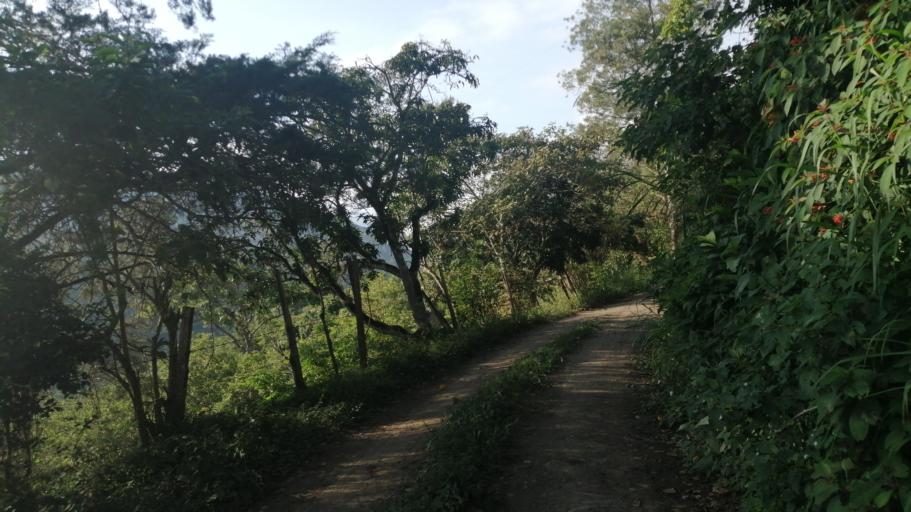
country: CO
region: Boyaca
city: Garagoa
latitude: 5.0753
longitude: -73.3883
